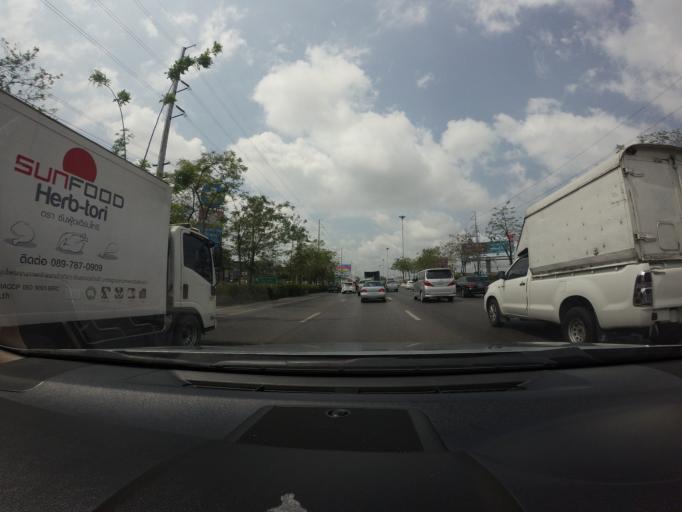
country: TH
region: Bangkok
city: Bang Khun Thian
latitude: 13.6679
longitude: 100.4487
